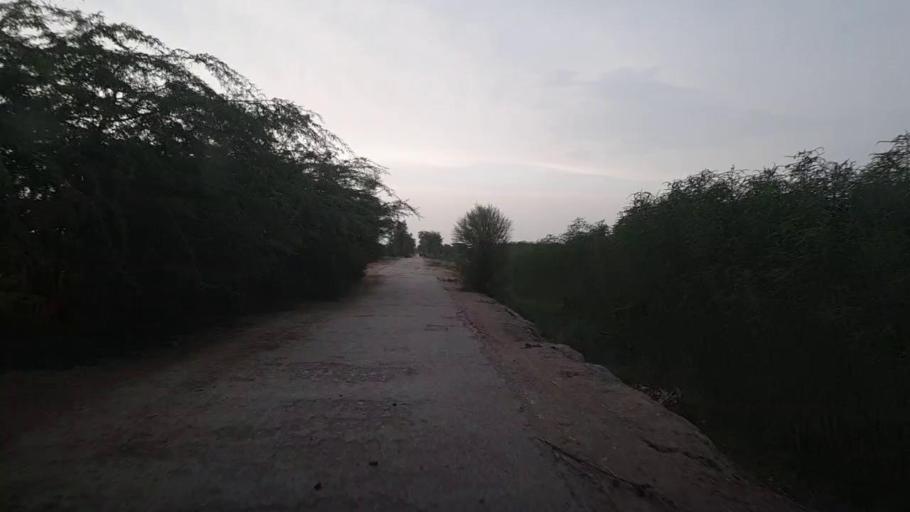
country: PK
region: Sindh
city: Karaundi
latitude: 27.0125
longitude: 68.3539
